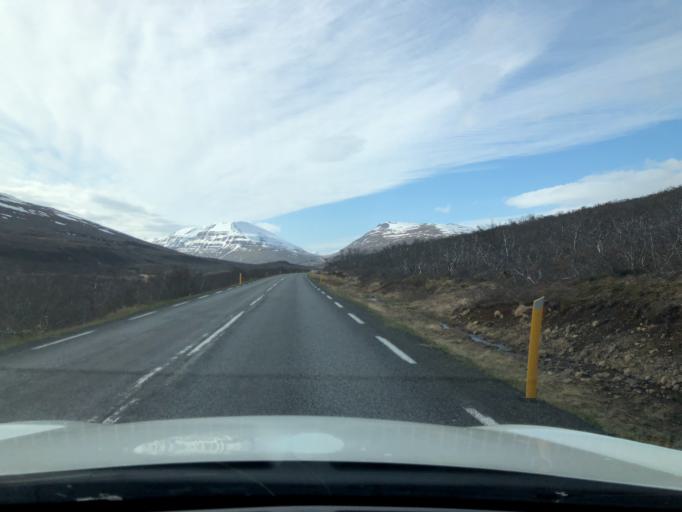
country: IS
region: East
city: Egilsstadir
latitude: 65.2380
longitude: -14.3476
